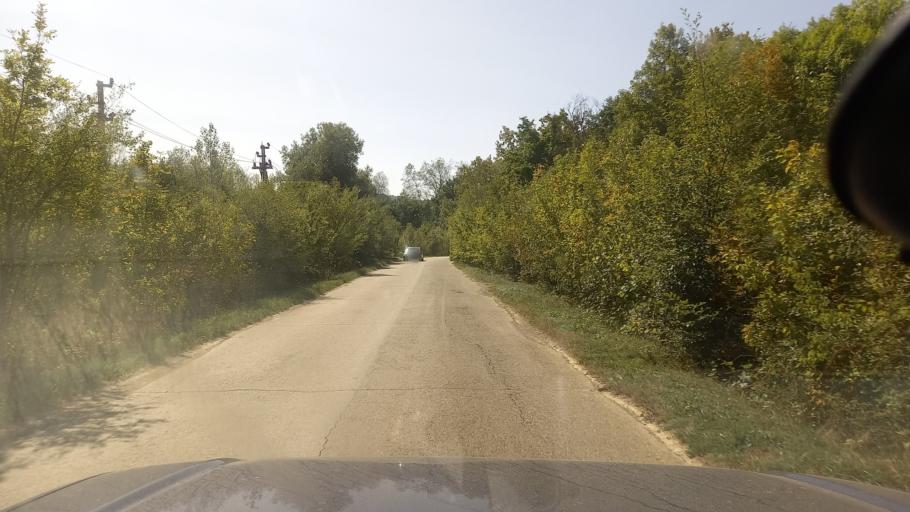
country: RU
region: Krasnodarskiy
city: Azovskaya
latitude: 44.7008
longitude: 38.6693
